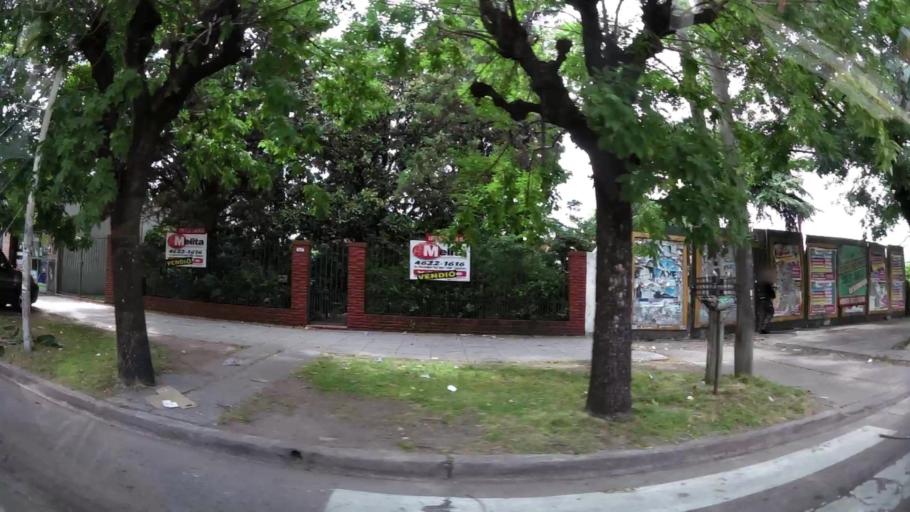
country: AR
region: Buenos Aires F.D.
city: Villa Lugano
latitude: -34.6892
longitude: -58.4971
